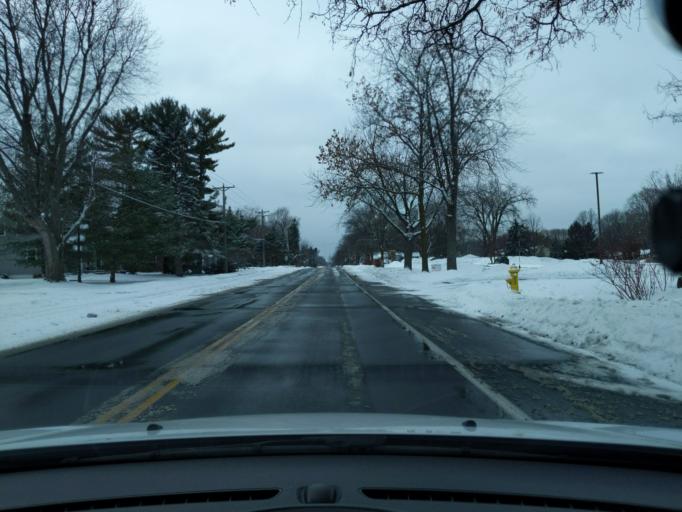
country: US
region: Minnesota
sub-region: Ramsey County
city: Roseville
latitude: 44.9993
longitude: -93.1496
